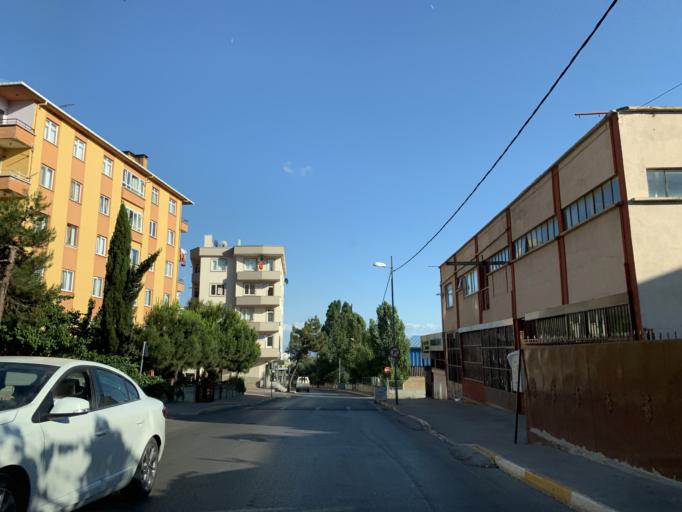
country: TR
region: Istanbul
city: Pendik
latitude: 40.9005
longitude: 29.2589
